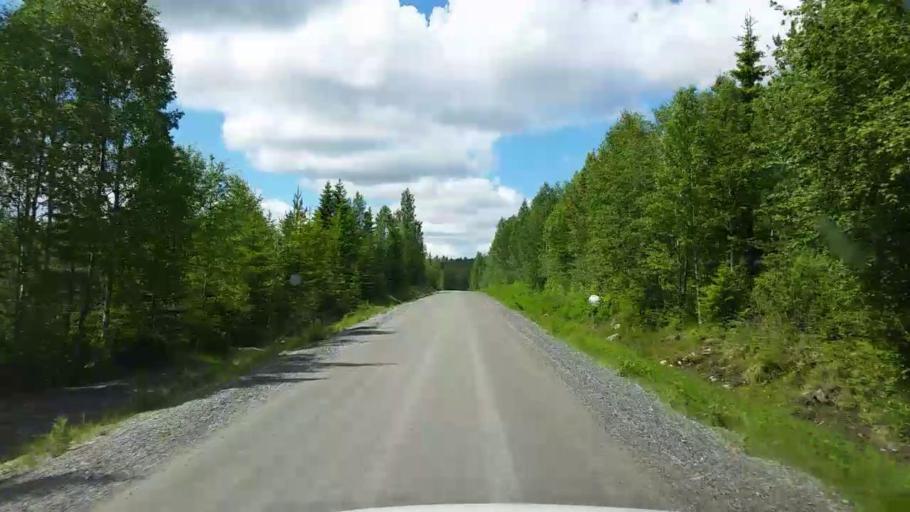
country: SE
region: Gaevleborg
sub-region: Bollnas Kommun
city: Vittsjo
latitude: 61.0903
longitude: 16.1817
